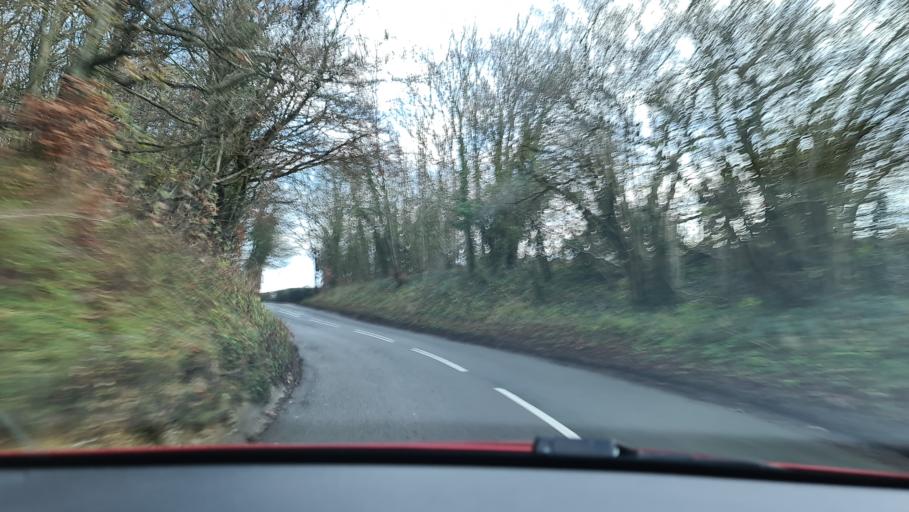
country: GB
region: England
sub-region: Buckinghamshire
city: Wendover
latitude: 51.7407
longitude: -0.7215
